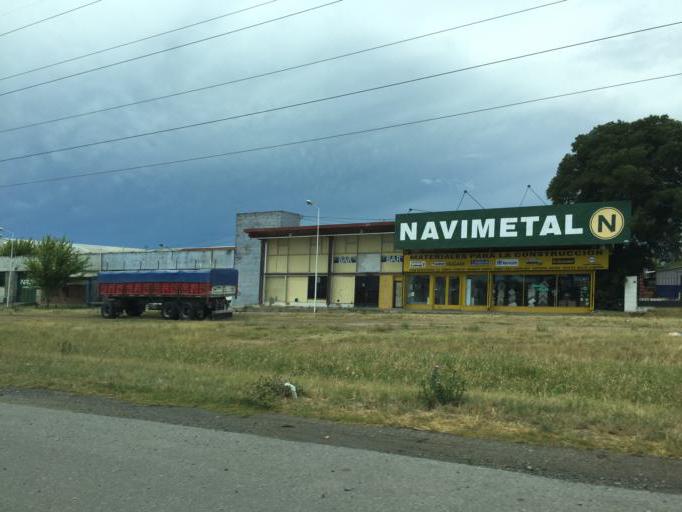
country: AR
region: Buenos Aires
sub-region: Partido de Tandil
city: Tandil
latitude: -37.3132
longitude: -59.1120
